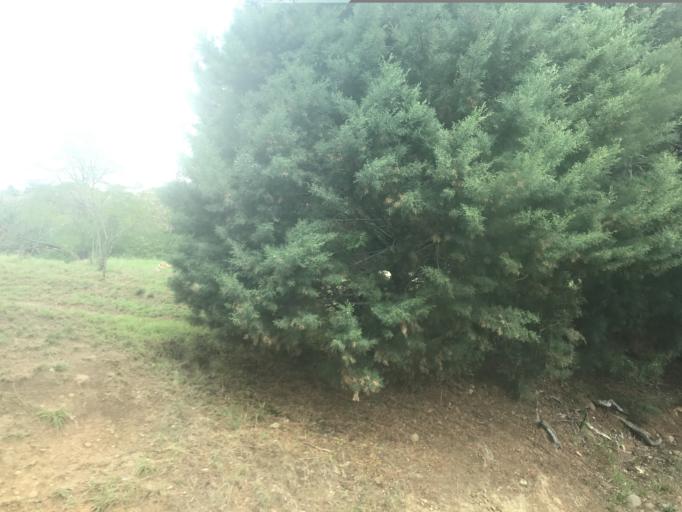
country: LS
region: Maseru
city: Nako
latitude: -29.6284
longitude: 27.5128
